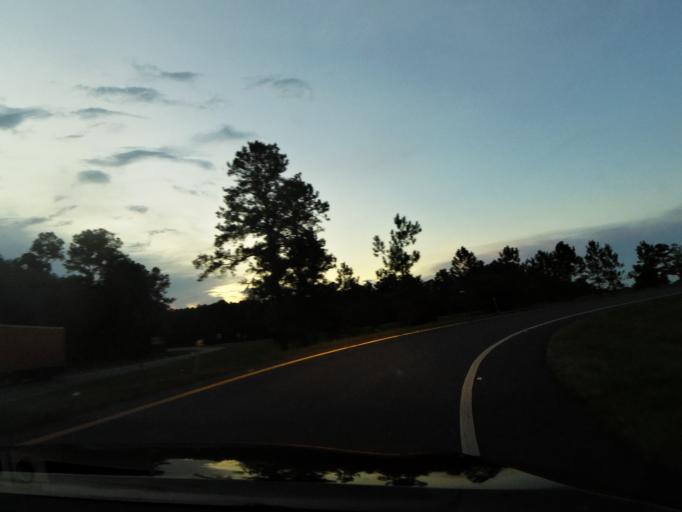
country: US
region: Florida
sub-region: Columbia County
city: Five Points
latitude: 30.2439
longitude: -82.6756
